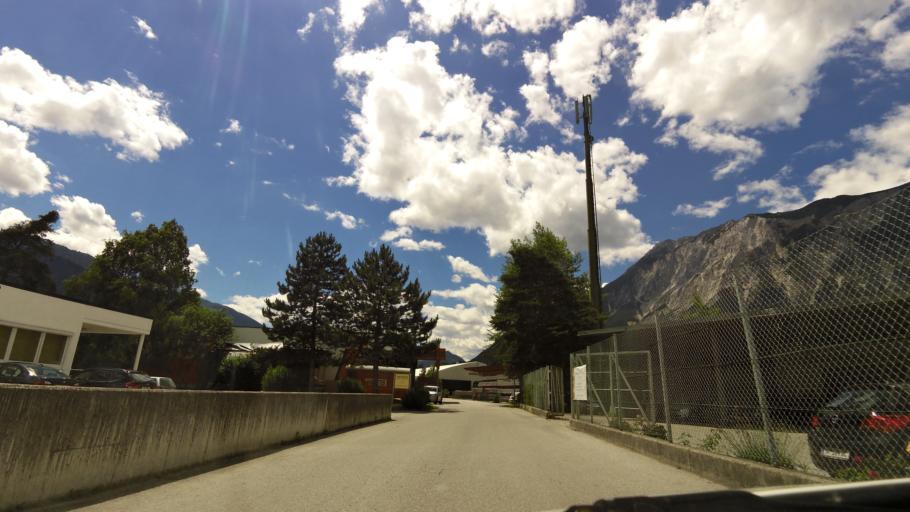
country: AT
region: Tyrol
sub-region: Politischer Bezirk Imst
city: Haiming
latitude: 47.2379
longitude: 10.8641
